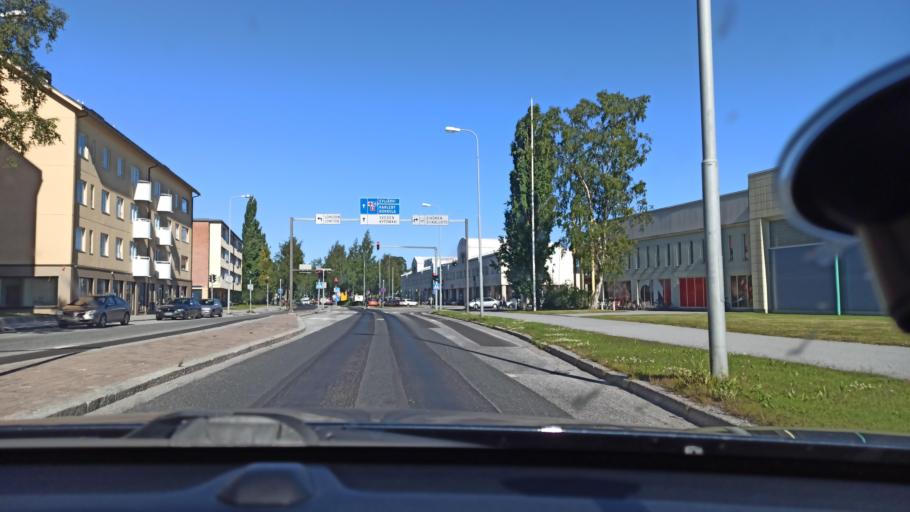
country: FI
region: Ostrobothnia
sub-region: Jakobstadsregionen
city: Jakobstad
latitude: 63.6779
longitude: 22.7130
